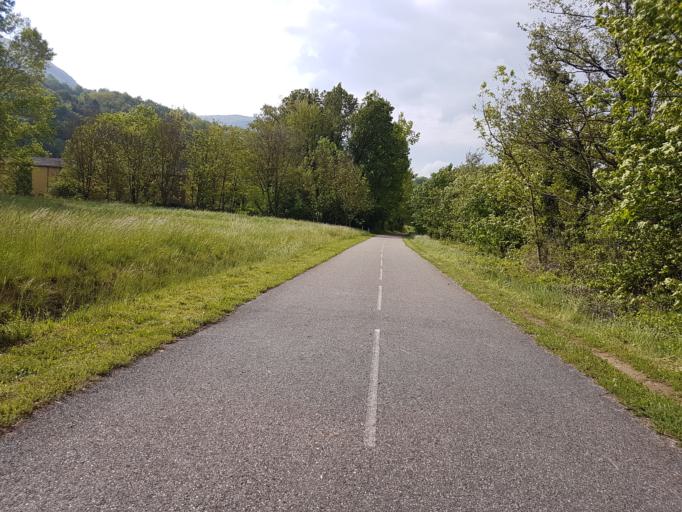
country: FR
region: Rhone-Alpes
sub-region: Departement de la Haute-Savoie
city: Versonnex
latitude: 45.9517
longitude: 5.8364
